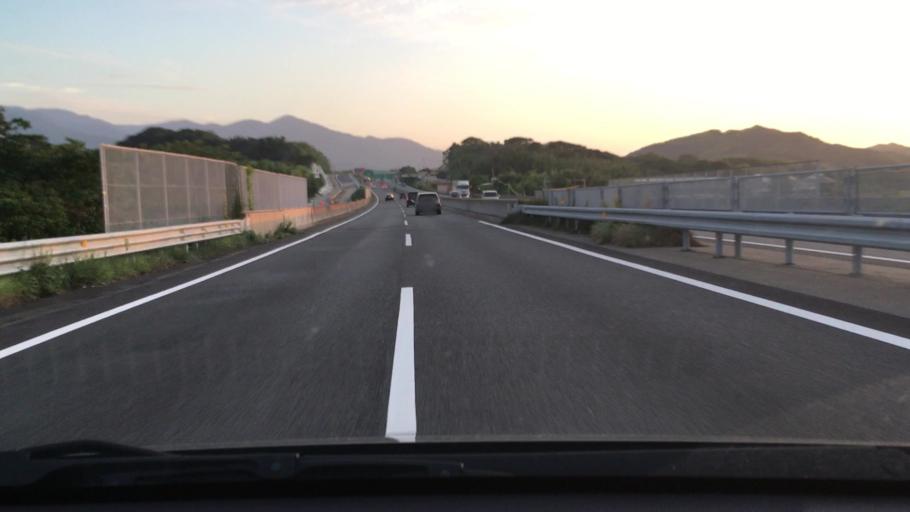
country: JP
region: Fukuoka
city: Maebaru-chuo
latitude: 33.5459
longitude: 130.2081
